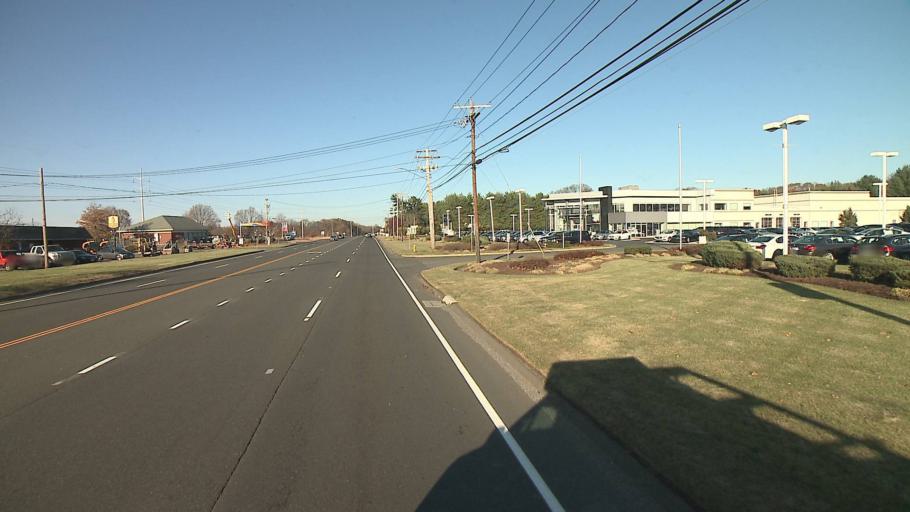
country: US
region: Connecticut
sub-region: New Haven County
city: Wallingford Center
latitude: 41.4209
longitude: -72.8397
